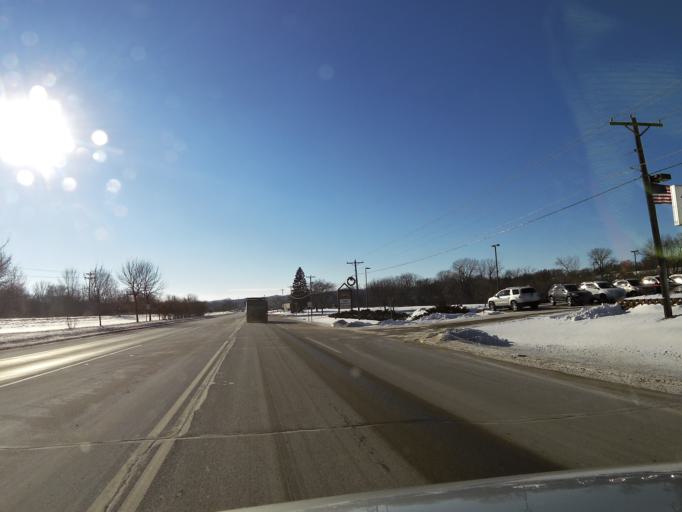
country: US
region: Minnesota
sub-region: Carver County
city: Chaska
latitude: 44.7944
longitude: -93.5924
